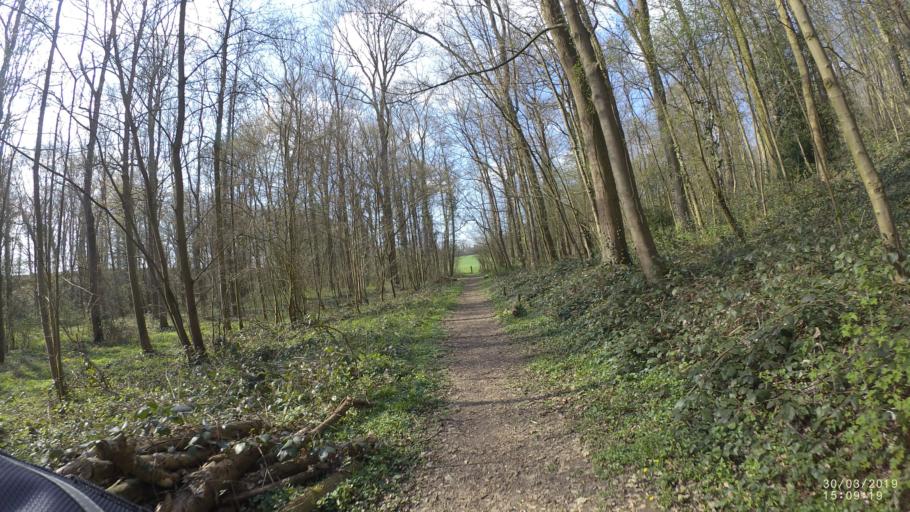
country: BE
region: Flanders
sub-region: Provincie Vlaams-Brabant
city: Overijse
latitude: 50.7572
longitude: 4.5574
